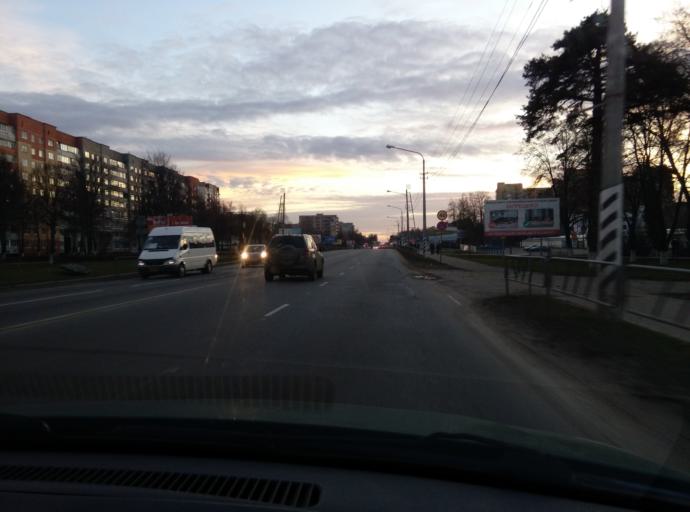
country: BY
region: Minsk
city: Horad Barysaw
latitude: 54.2227
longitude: 28.4931
